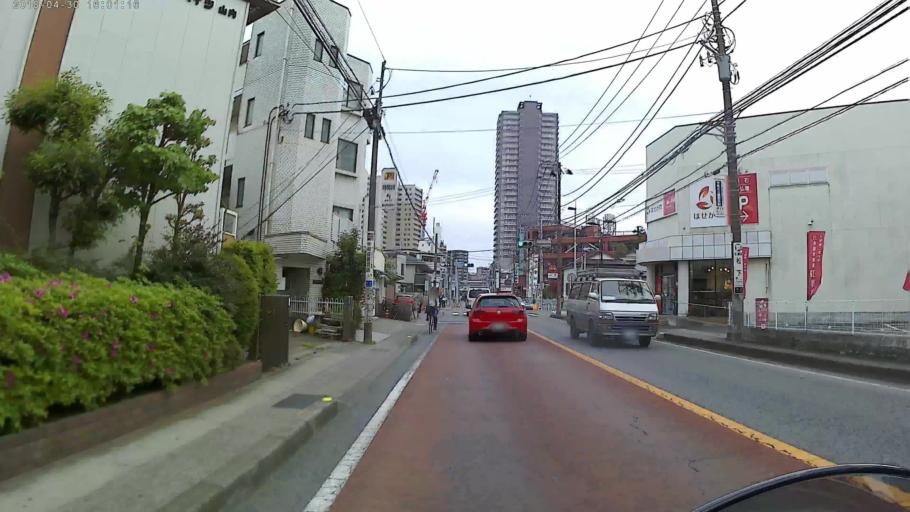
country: JP
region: Tokyo
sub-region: Machida-shi
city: Machida
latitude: 35.5179
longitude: 139.4228
